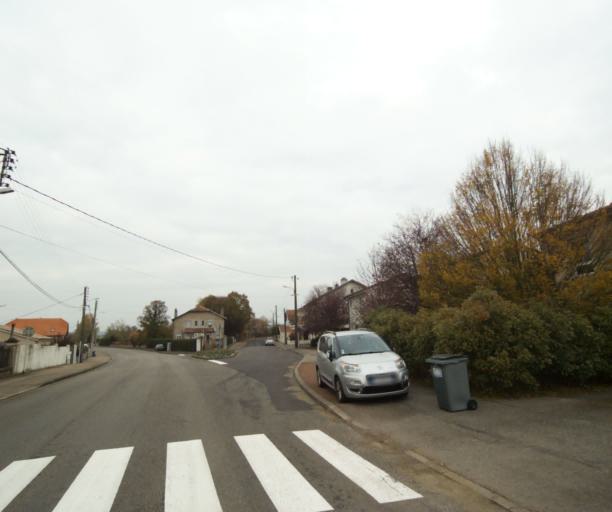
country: FR
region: Lorraine
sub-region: Departement de Meurthe-et-Moselle
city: Mancieulles
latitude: 49.2867
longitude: 5.8939
